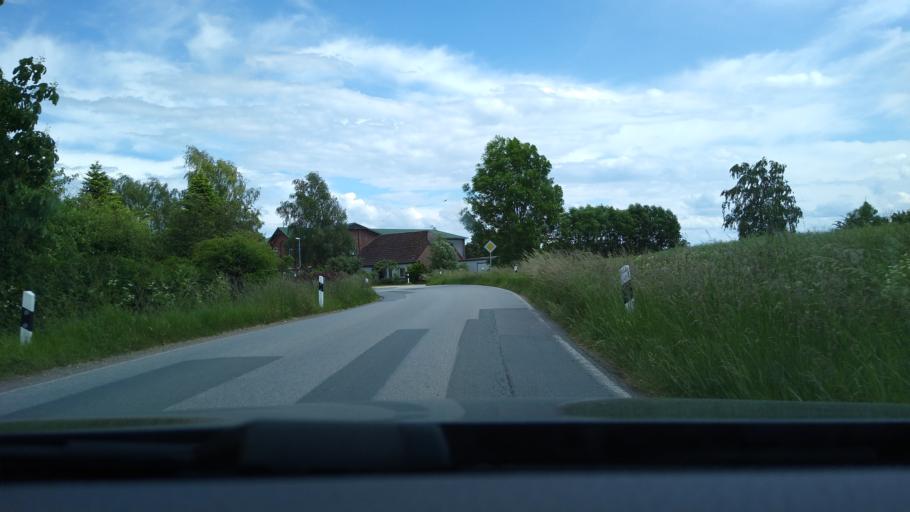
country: DE
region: Schleswig-Holstein
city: Riepsdorf
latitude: 54.2205
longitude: 10.9694
